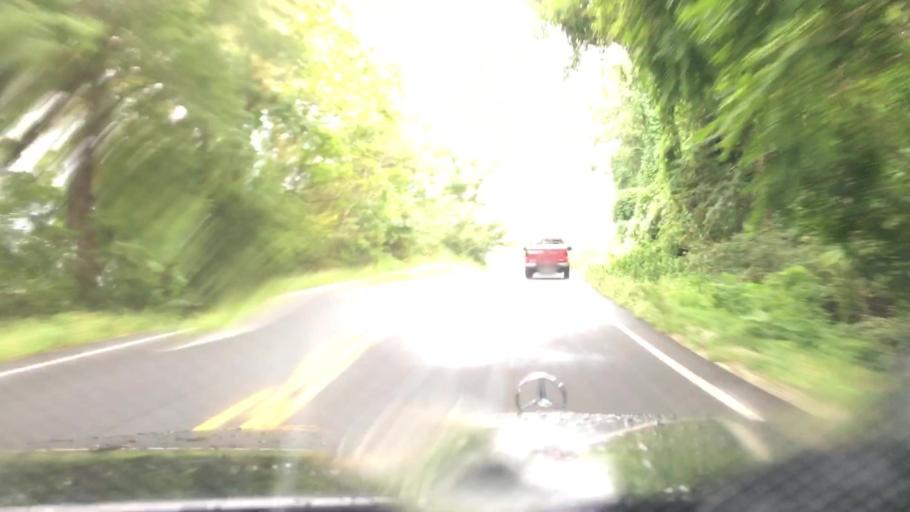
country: US
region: Virginia
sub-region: Nelson County
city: Nellysford
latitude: 37.8999
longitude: -78.8592
